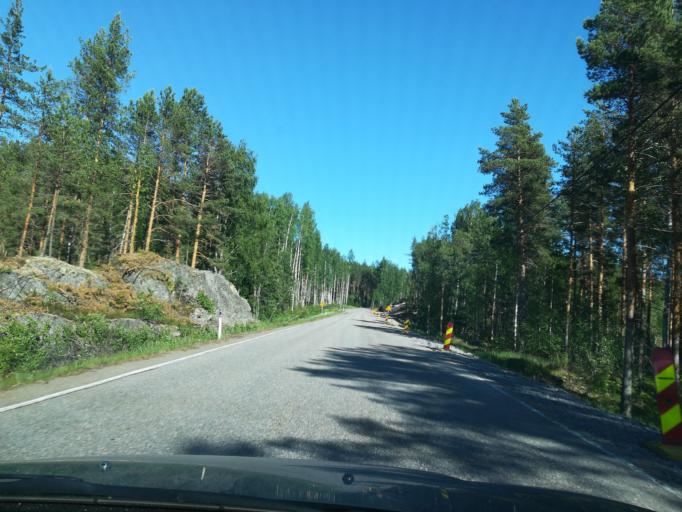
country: FI
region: Southern Savonia
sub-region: Mikkeli
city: Puumala
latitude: 61.4678
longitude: 28.3212
